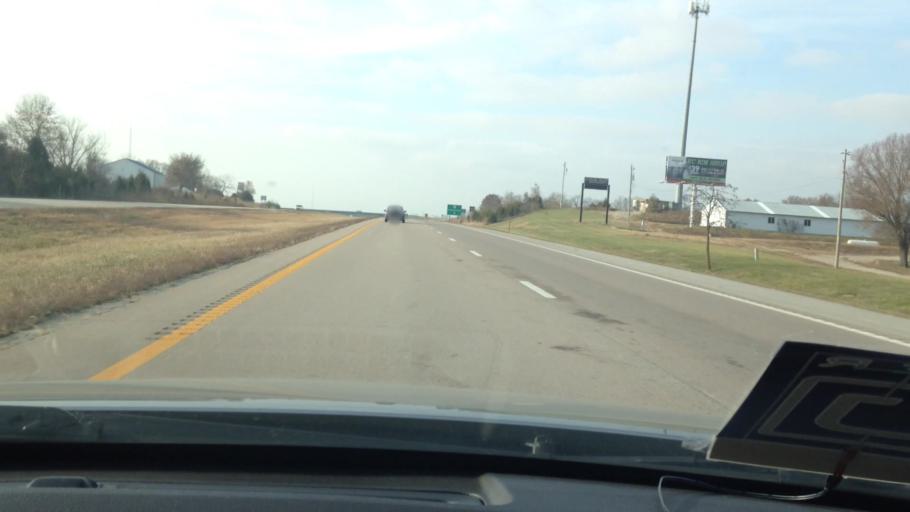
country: US
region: Missouri
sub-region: Cass County
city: Garden City
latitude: 38.4974
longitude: -94.0642
